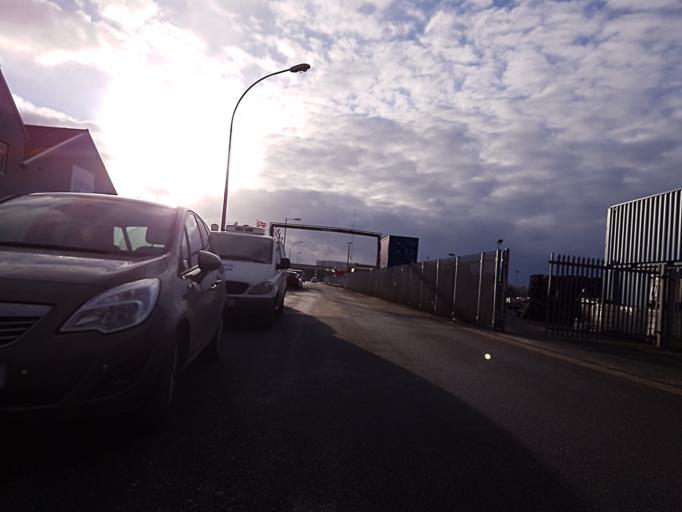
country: GB
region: England
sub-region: North East Lincolnshire
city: Grimsby
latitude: 53.5798
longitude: -0.0593
